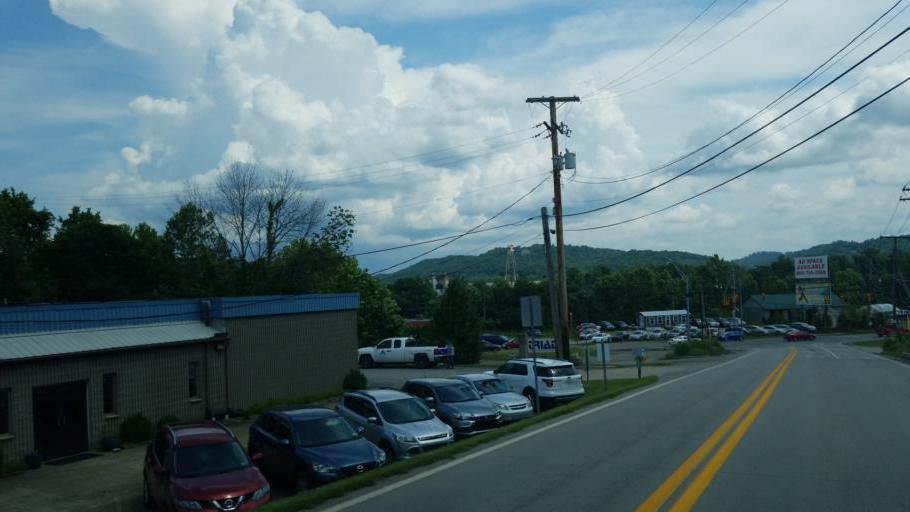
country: US
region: West Virginia
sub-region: Kanawha County
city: Nitro
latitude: 38.4356
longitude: -81.8540
